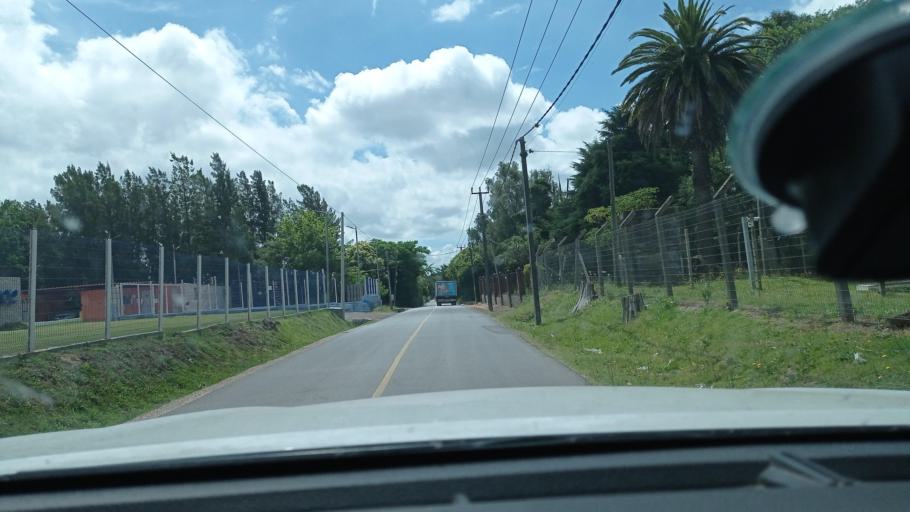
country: UY
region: Canelones
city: La Paz
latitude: -34.8086
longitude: -56.1987
